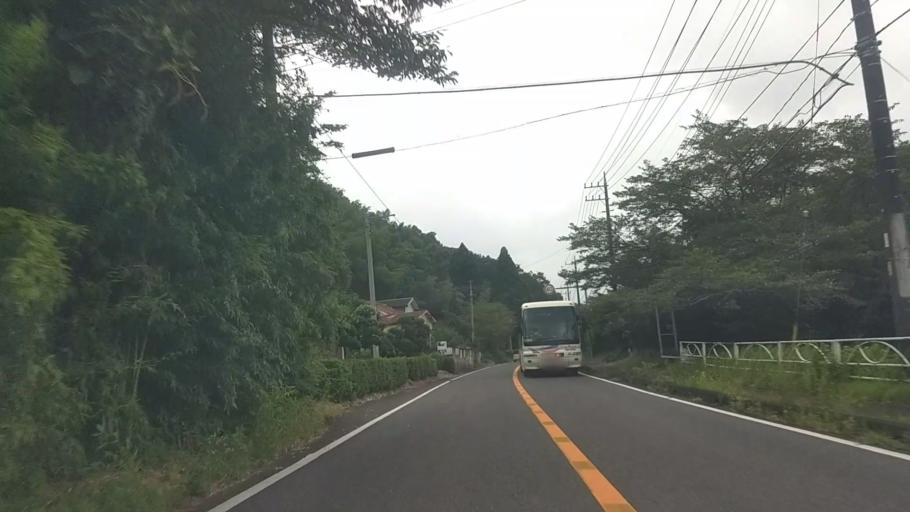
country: JP
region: Chiba
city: Kisarazu
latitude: 35.3044
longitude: 140.0717
